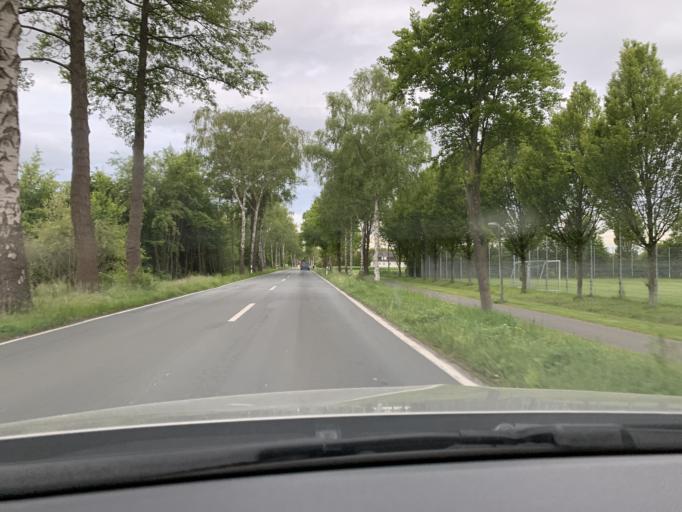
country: DE
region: North Rhine-Westphalia
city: Rietberg
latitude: 51.8362
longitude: 8.3669
